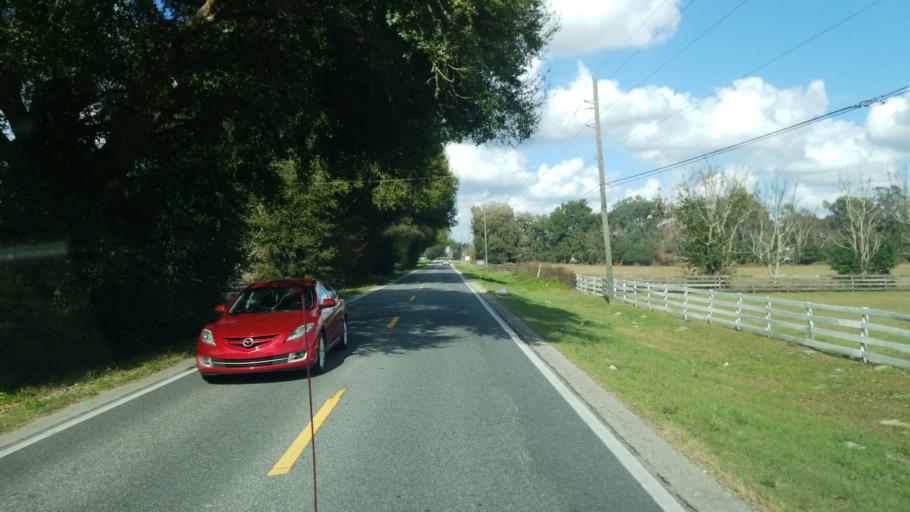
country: US
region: Florida
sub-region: Marion County
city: Belleview
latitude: 28.9869
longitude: -82.1199
